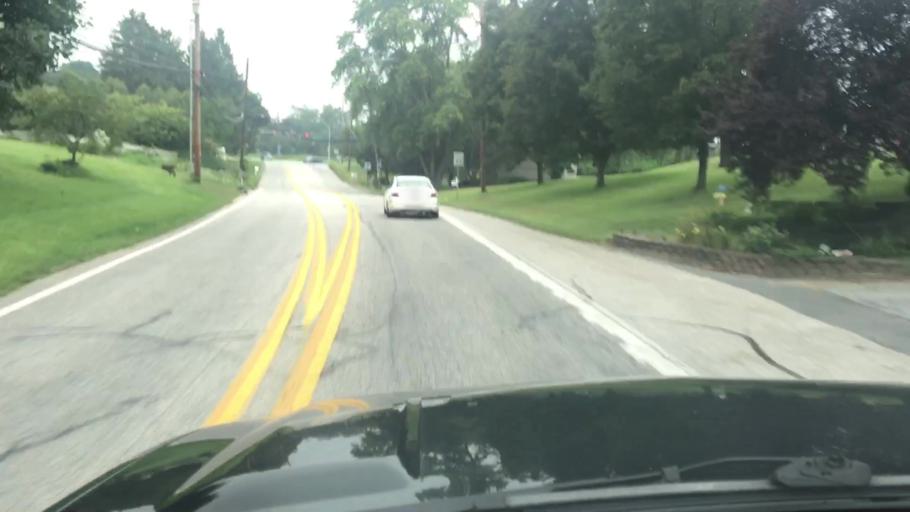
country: US
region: Pennsylvania
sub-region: Cumberland County
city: Shiremanstown
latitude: 40.2652
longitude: -76.9787
